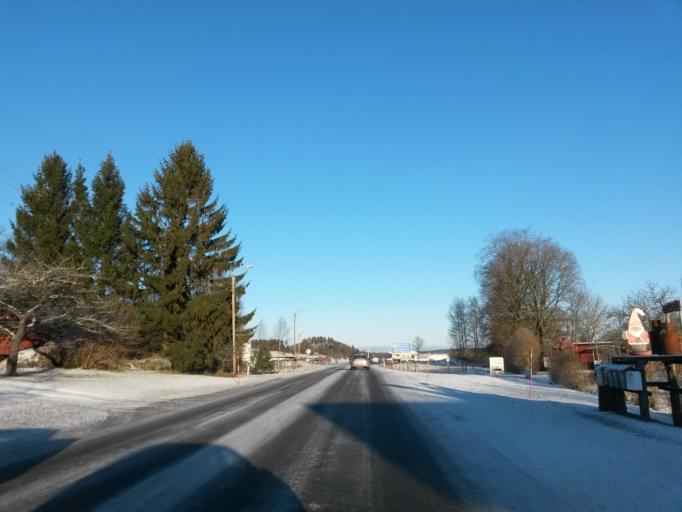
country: SE
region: Vaestra Goetaland
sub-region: Vargarda Kommun
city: Vargarda
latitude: 58.0486
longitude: 12.8159
